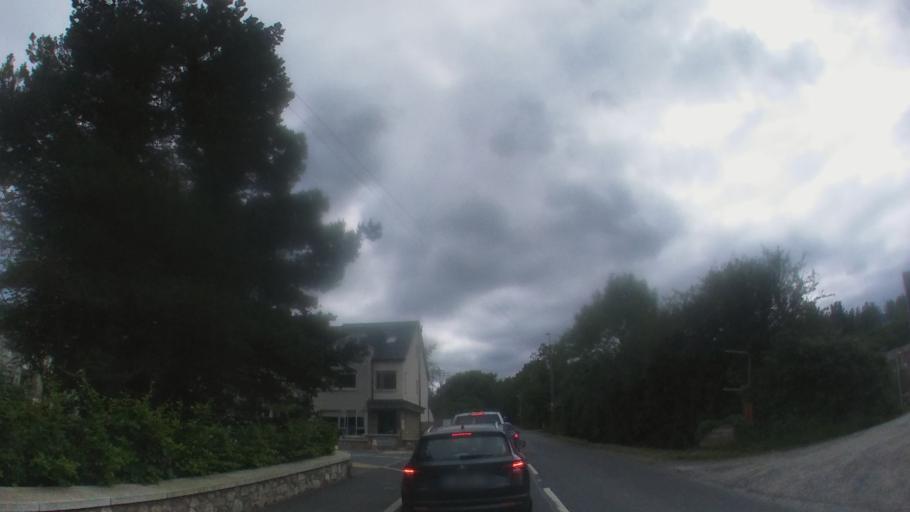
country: IE
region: Leinster
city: Foxrock
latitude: 53.2446
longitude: -6.1876
